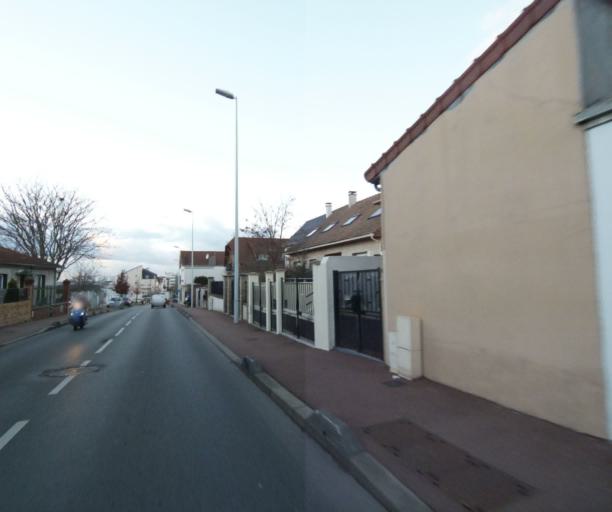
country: FR
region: Ile-de-France
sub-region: Departement des Hauts-de-Seine
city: Nanterre
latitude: 48.8848
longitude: 2.2132
